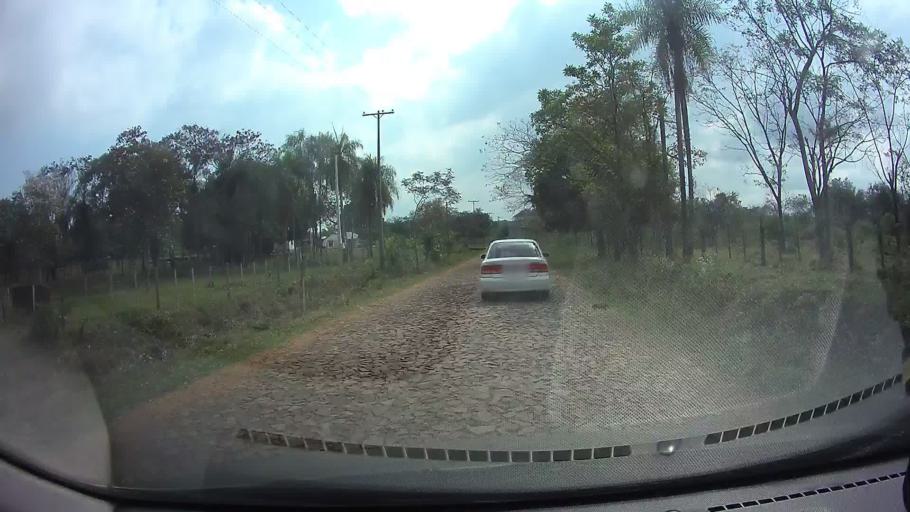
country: PY
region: Cordillera
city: Arroyos y Esteros
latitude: -24.9966
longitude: -57.1842
